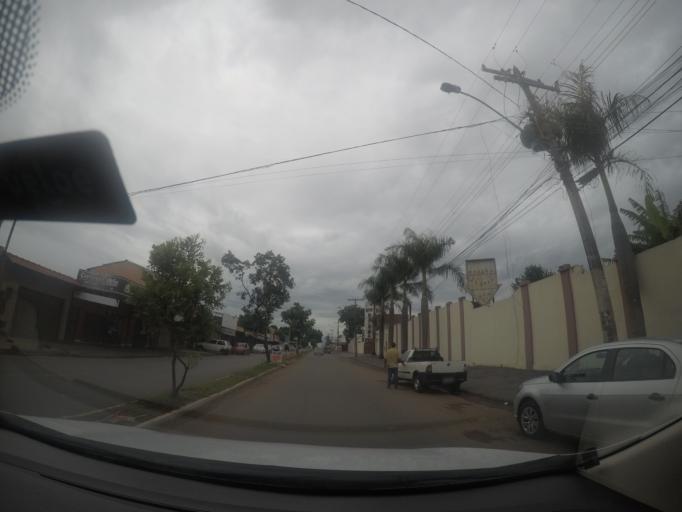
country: BR
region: Goias
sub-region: Goiania
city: Goiania
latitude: -16.6673
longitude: -49.3240
